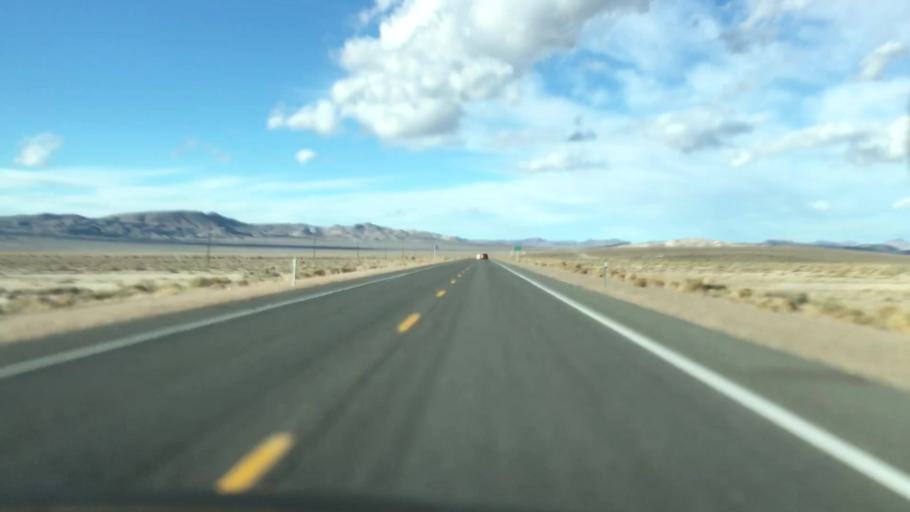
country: US
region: Nevada
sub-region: Esmeralda County
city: Goldfield
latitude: 37.4552
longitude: -117.1703
